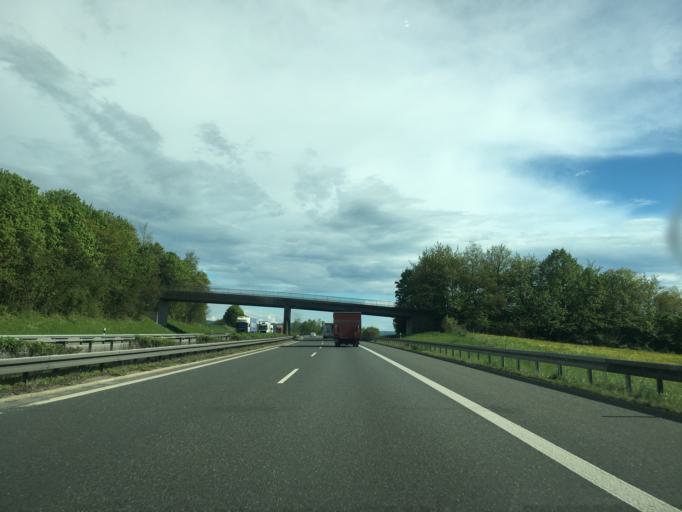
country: DE
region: Bavaria
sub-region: Upper Palatinate
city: Pilsach
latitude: 49.3317
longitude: 11.4544
